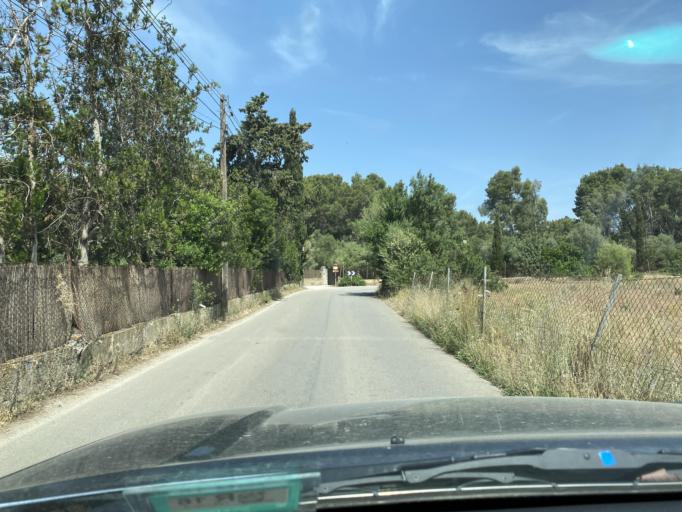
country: ES
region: Balearic Islands
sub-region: Illes Balears
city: Marratxi
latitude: 39.6240
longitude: 2.7103
